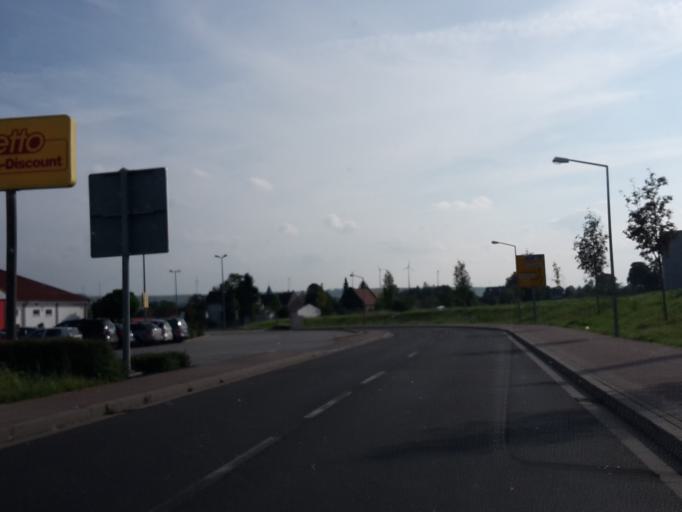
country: DE
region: Rheinland-Pfalz
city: Gau-Odernheim
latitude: 49.7781
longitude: 8.1895
